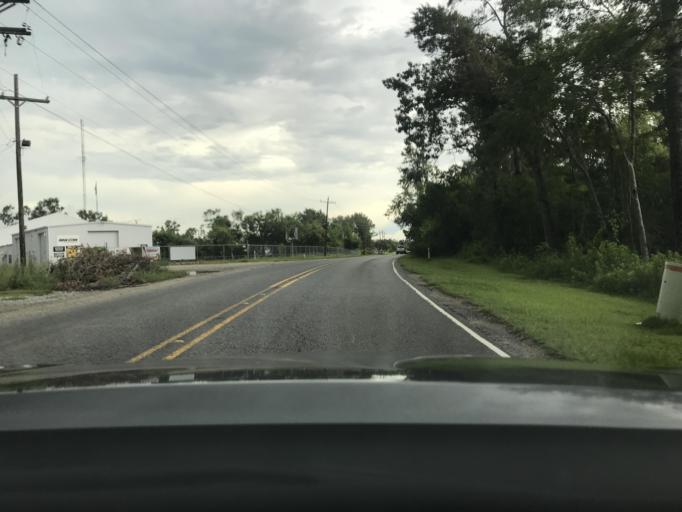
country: US
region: Louisiana
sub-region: Calcasieu Parish
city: Westlake
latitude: 30.2481
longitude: -93.2502
